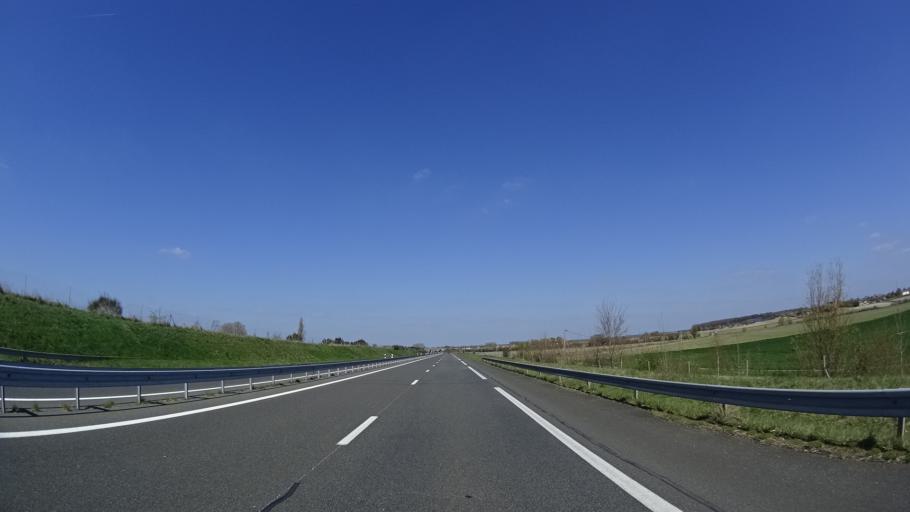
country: FR
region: Pays de la Loire
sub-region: Departement de Maine-et-Loire
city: Saint-Jean
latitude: 47.2662
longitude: -0.3349
